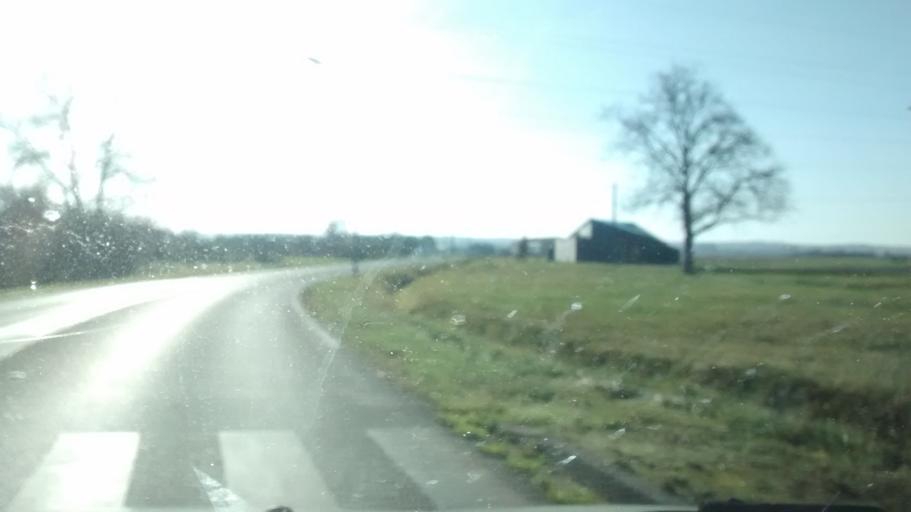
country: FR
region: Centre
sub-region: Departement d'Indre-et-Loire
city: Nazelles-Negron
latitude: 47.4274
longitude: 0.9592
